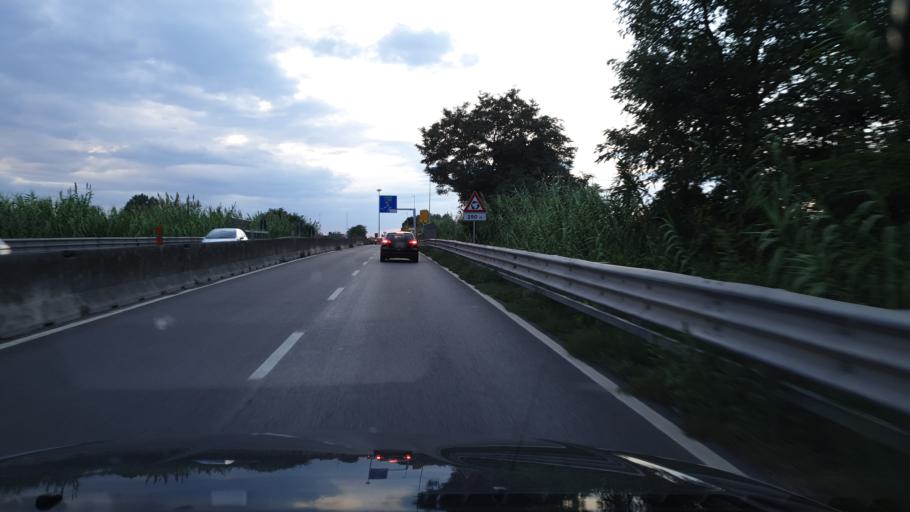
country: IT
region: Emilia-Romagna
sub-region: Provincia di Ravenna
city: Madonna Dell'Albero
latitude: 44.3835
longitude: 12.1977
